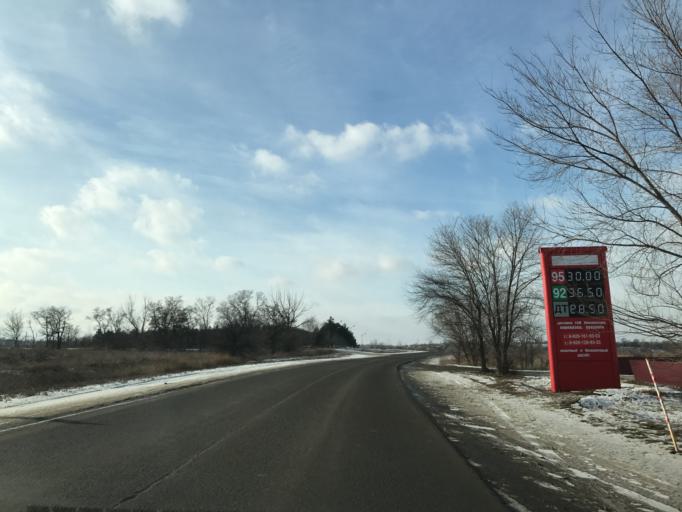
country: RU
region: Rostov
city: Staraya Stanitsa
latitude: 48.2412
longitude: 40.4123
